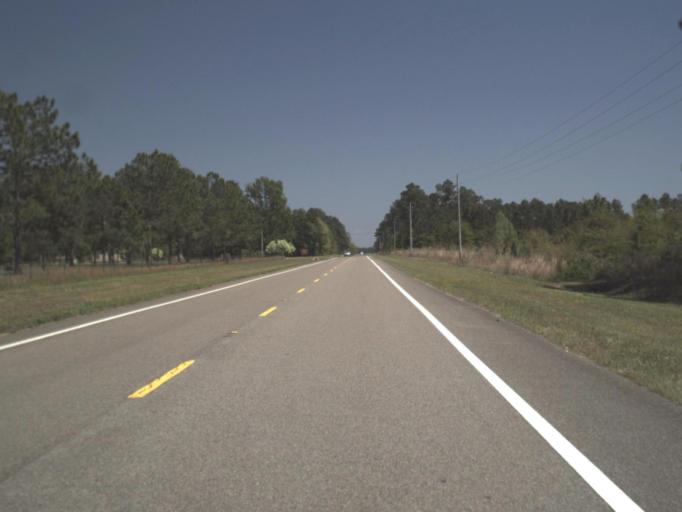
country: US
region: Florida
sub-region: Santa Rosa County
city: Point Baker
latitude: 30.8574
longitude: -86.8692
